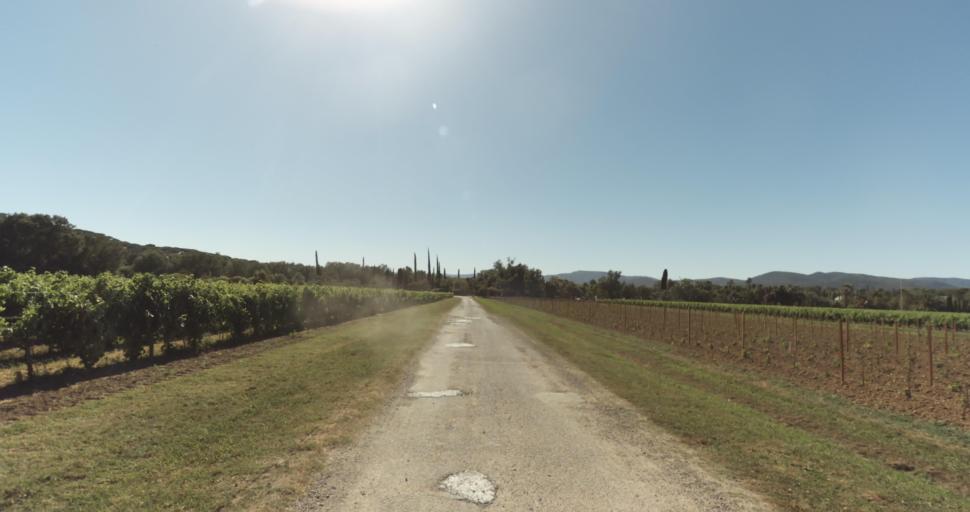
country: FR
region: Provence-Alpes-Cote d'Azur
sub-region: Departement du Var
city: Gassin
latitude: 43.2538
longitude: 6.5950
